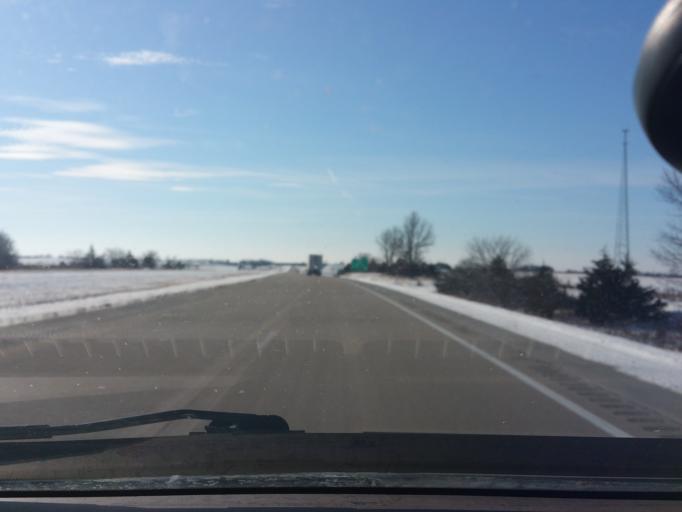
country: US
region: Iowa
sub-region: Decatur County
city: Leon
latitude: 40.8189
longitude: -93.8242
